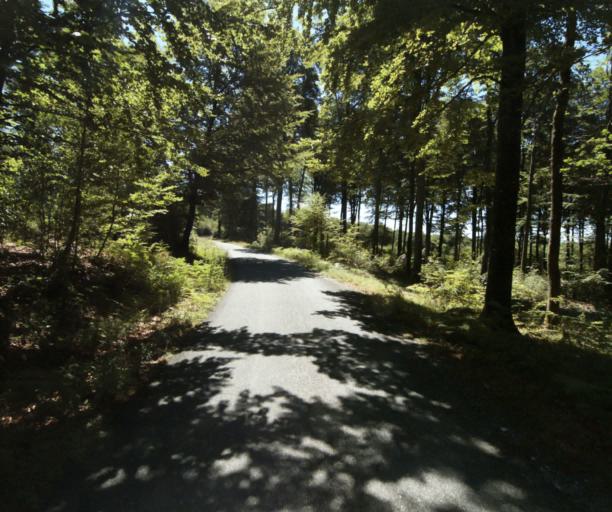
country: FR
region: Midi-Pyrenees
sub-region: Departement du Tarn
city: Dourgne
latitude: 43.4153
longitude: 2.1868
